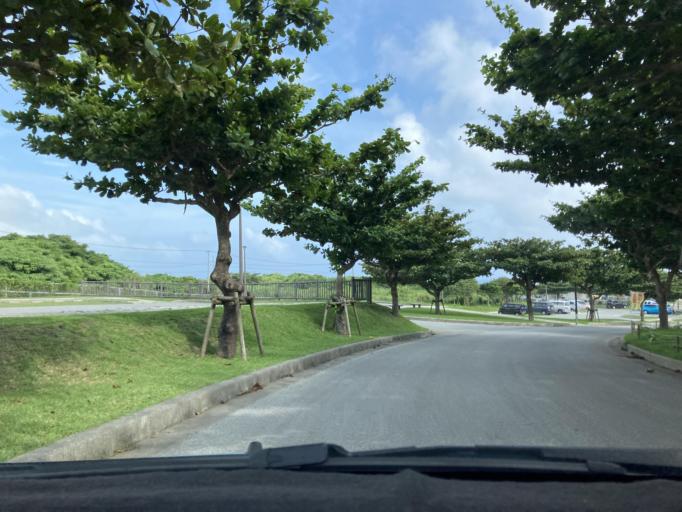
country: JP
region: Okinawa
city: Itoman
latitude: 26.0991
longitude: 127.7256
